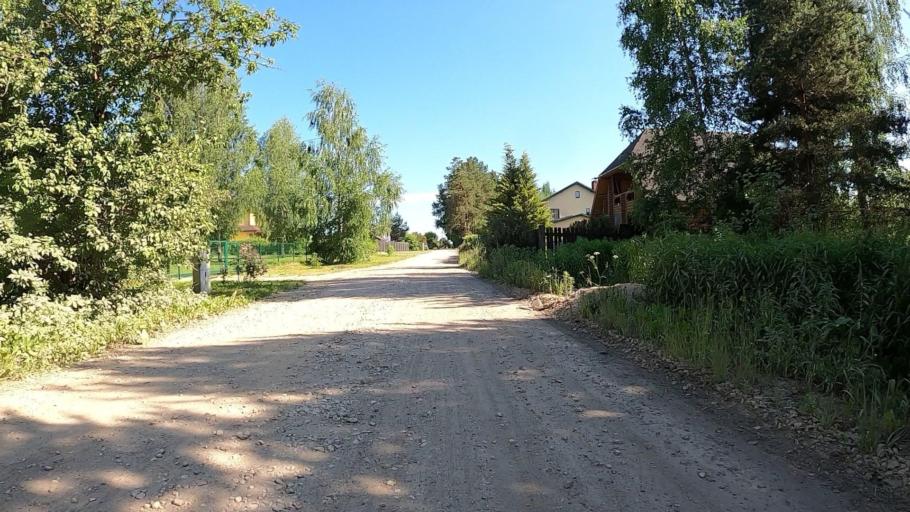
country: LV
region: Stopini
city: Ulbroka
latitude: 56.9104
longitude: 24.3131
